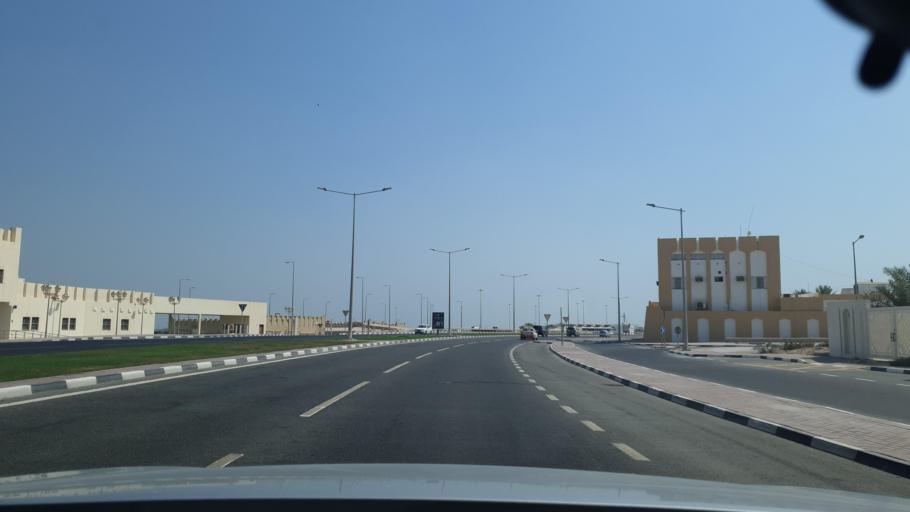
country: QA
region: Al Khawr
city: Al Khawr
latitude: 25.6864
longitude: 51.5125
